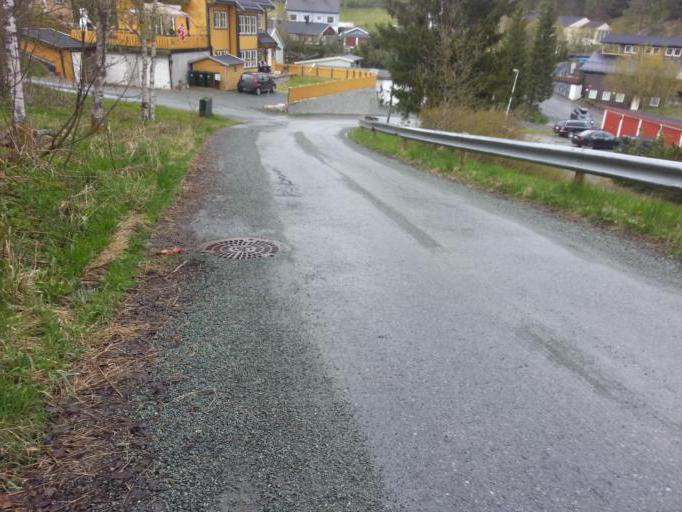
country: NO
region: Sor-Trondelag
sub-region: Trondheim
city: Trondheim
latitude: 63.3939
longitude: 10.3531
